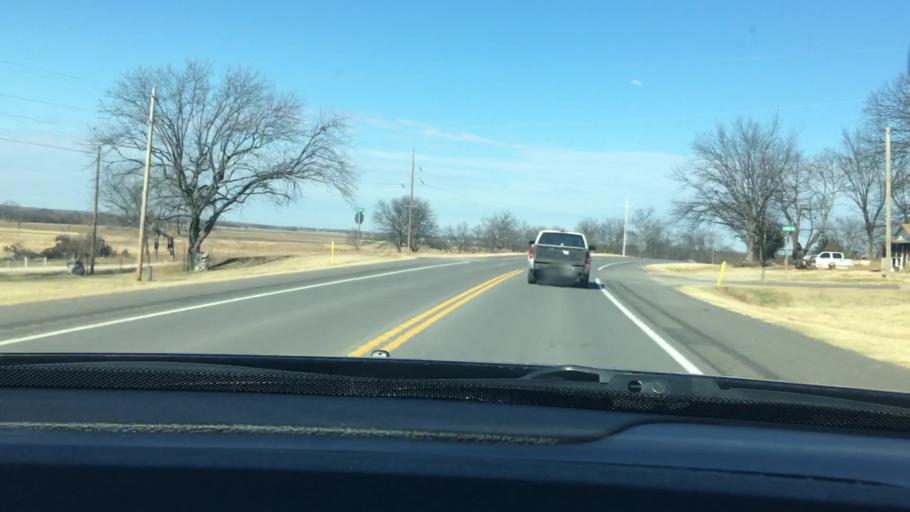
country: US
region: Oklahoma
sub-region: Garvin County
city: Wynnewood
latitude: 34.5788
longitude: -97.1418
